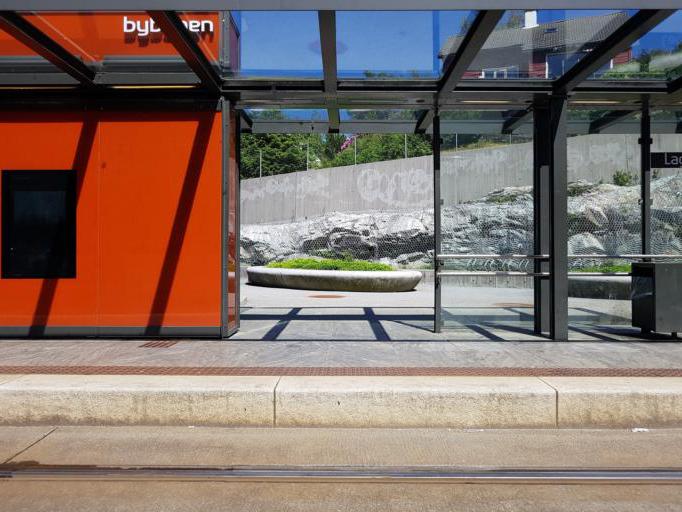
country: NO
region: Hordaland
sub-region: Bergen
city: Sandsli
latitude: 60.2982
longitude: 5.3291
